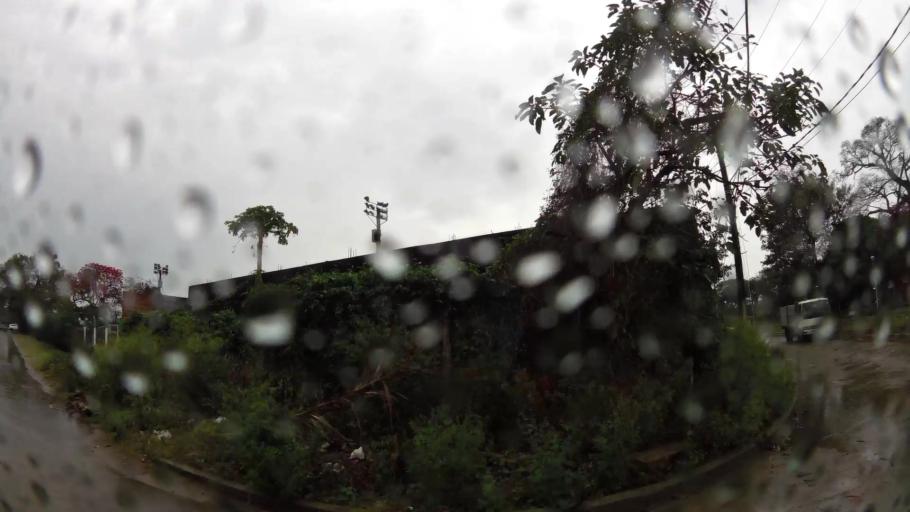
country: BO
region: Santa Cruz
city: Santa Cruz de la Sierra
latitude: -17.7890
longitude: -63.2227
